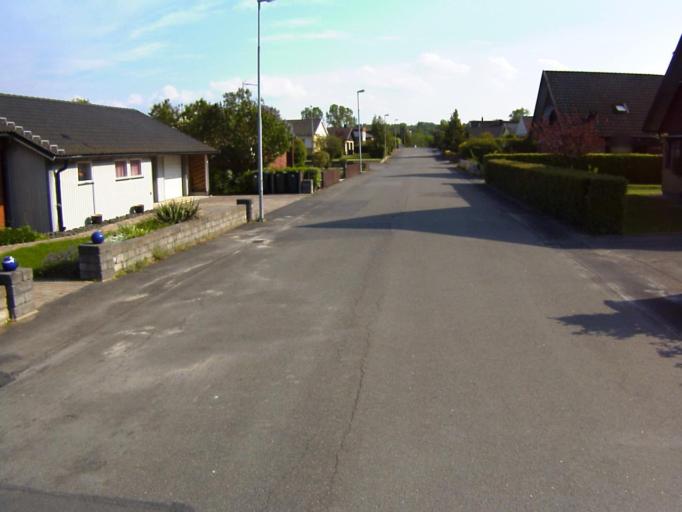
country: SE
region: Skane
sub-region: Kristianstads Kommun
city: Onnestad
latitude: 56.0552
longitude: 14.0216
